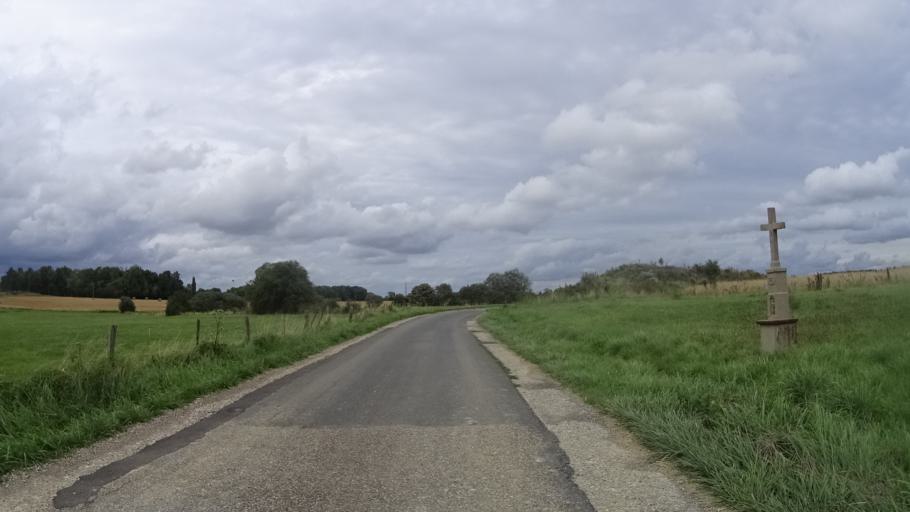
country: FR
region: Lorraine
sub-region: Departement de la Moselle
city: Niderviller
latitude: 48.7067
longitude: 7.0864
